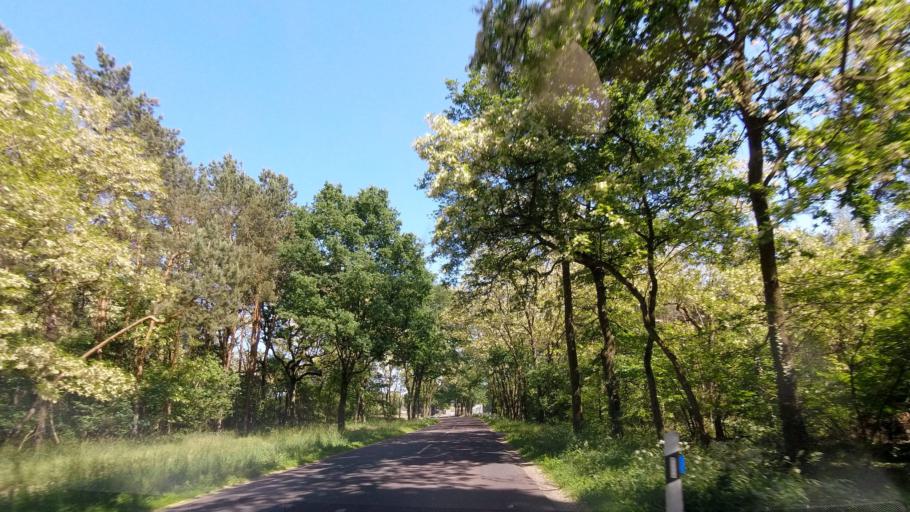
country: DE
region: Brandenburg
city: Gross Kreutz
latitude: 52.3641
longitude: 12.7344
